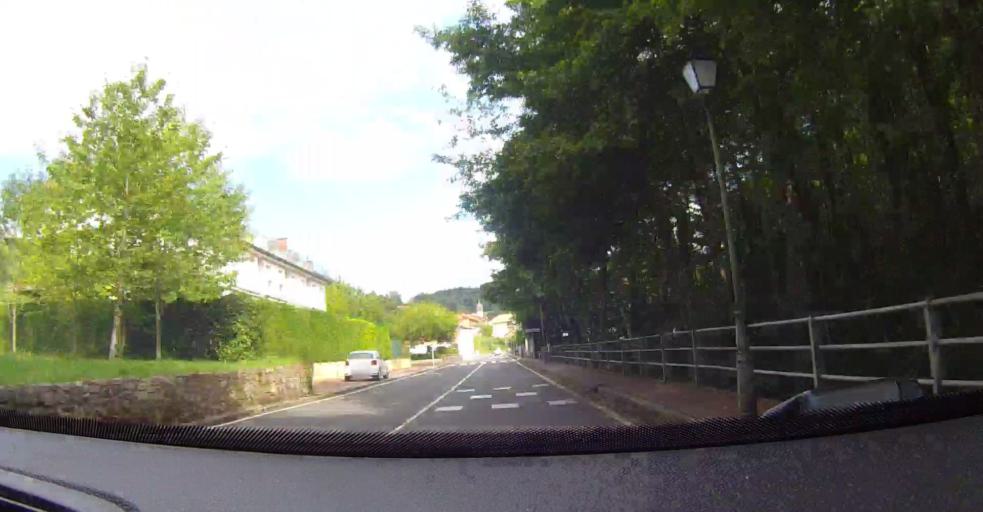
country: ES
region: Basque Country
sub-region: Bizkaia
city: Ibarrangelu
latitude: 43.3917
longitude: -2.6385
